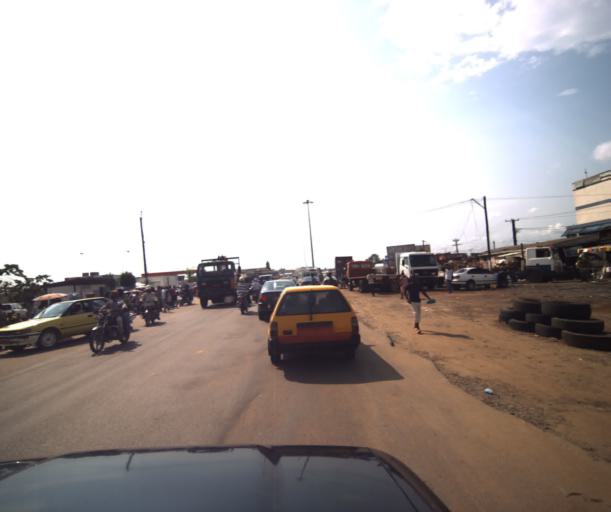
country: CM
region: Littoral
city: Douala
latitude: 4.0115
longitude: 9.7332
